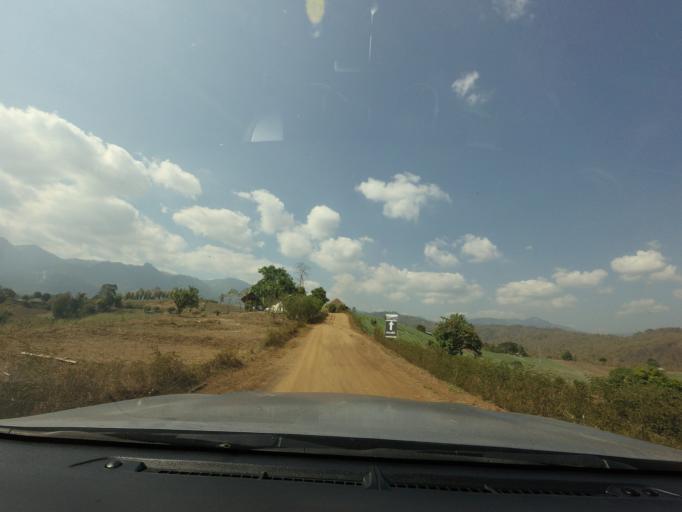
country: TH
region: Mae Hong Son
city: Wiang Nuea
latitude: 19.4003
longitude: 98.4099
